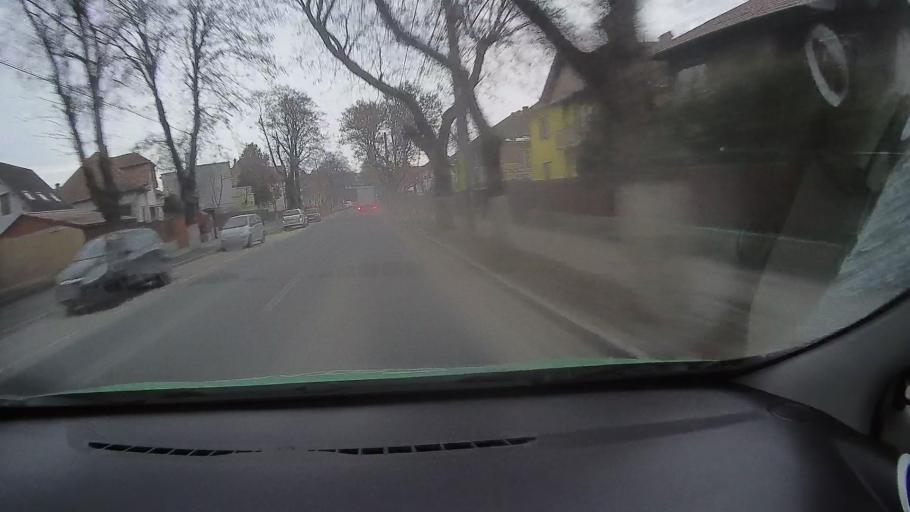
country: RO
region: Harghita
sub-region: Municipiul Odorheiu Secuiesc
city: Odorheiu Secuiesc
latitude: 46.3123
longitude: 25.2871
